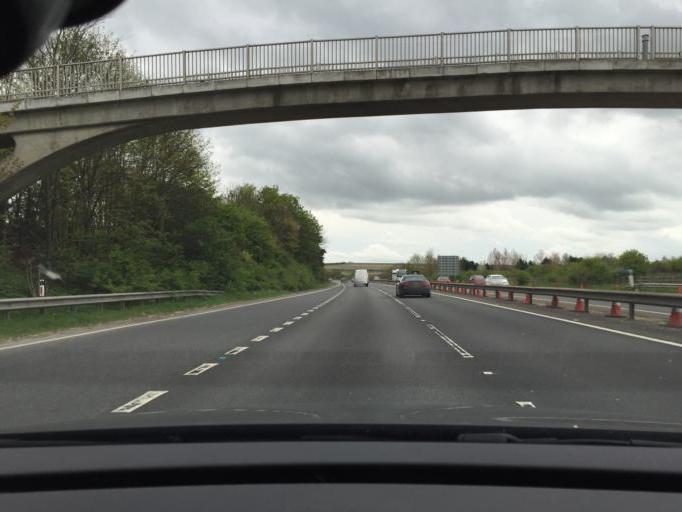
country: GB
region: England
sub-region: Oxfordshire
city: Harwell
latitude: 51.5698
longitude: -1.2994
